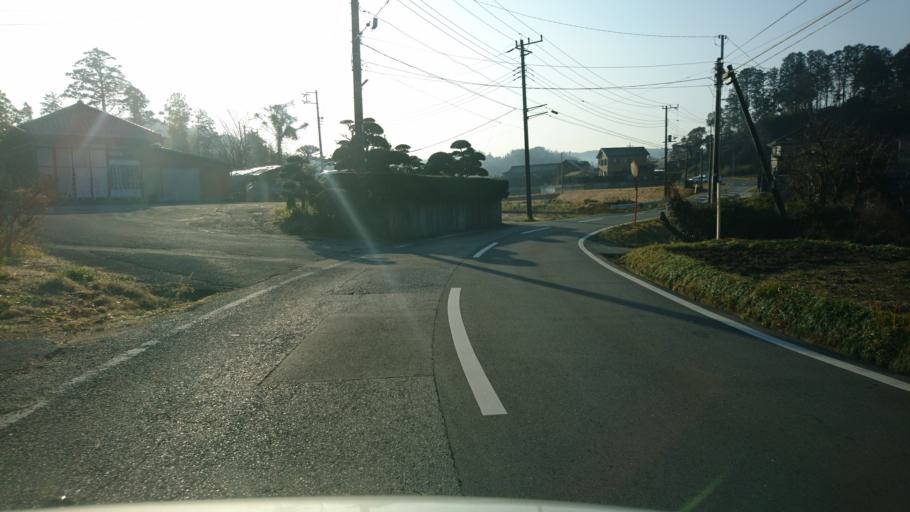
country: JP
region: Chiba
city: Kimitsu
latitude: 35.3029
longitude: 139.9477
